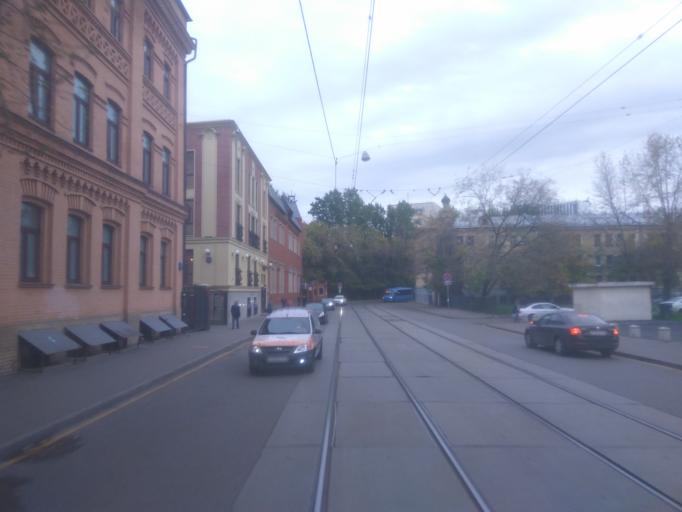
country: RU
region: Moscow
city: Lefortovo
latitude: 55.7760
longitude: 37.6767
